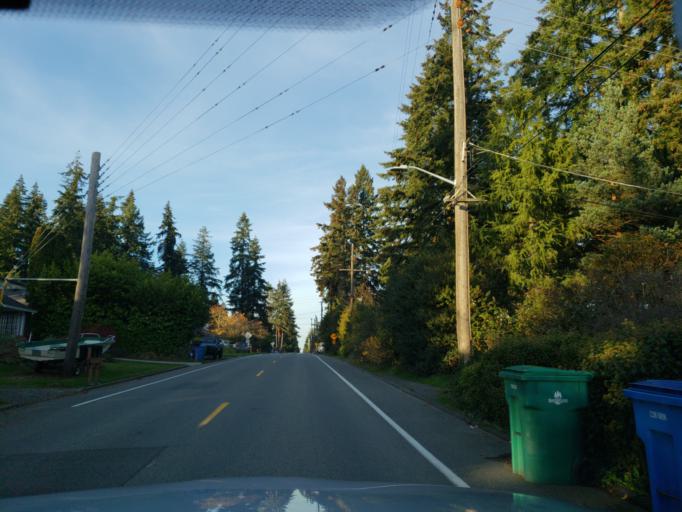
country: US
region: Washington
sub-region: King County
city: Shoreline
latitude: 47.7468
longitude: -122.3400
